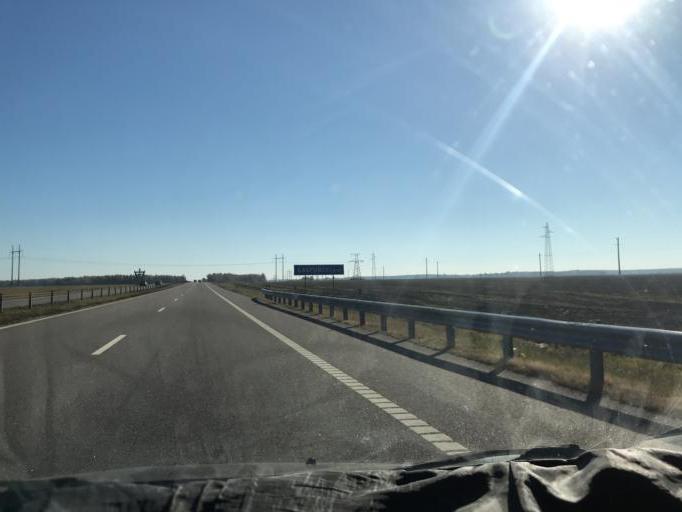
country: BY
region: Mogilev
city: Yalizava
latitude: 53.2307
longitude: 28.9887
